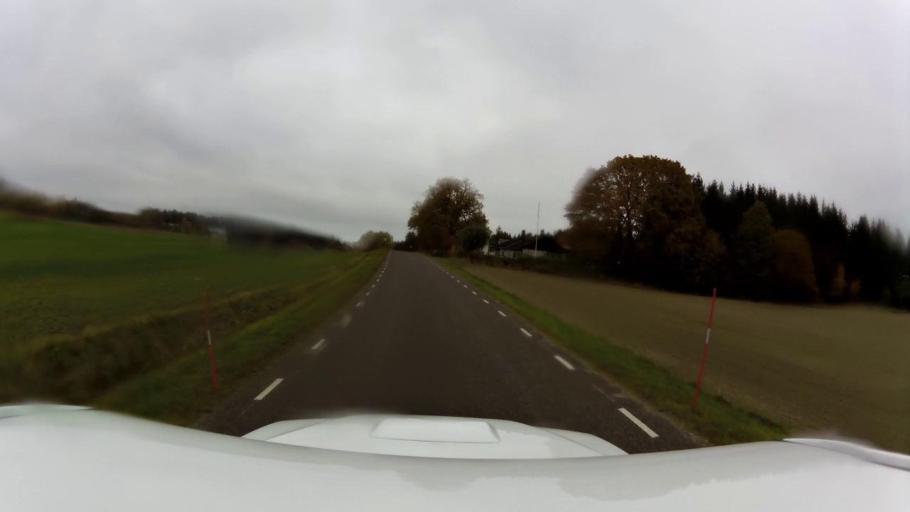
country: SE
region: OEstergoetland
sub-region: Linkopings Kommun
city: Linghem
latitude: 58.4647
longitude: 15.7716
